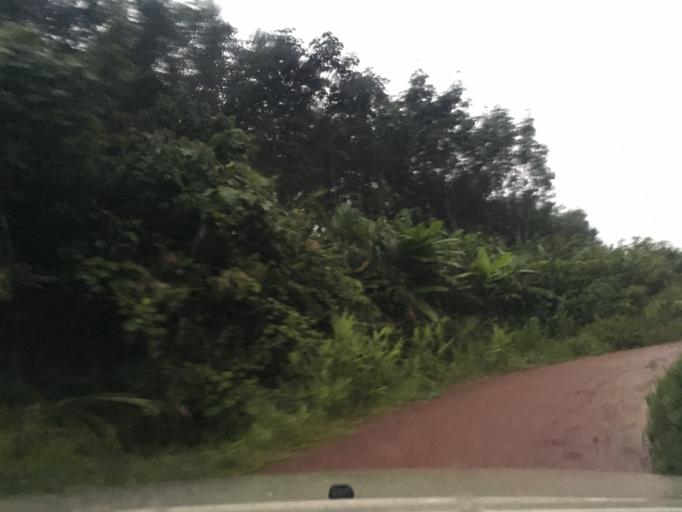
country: LA
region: Oudomxai
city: Muang La
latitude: 21.2490
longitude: 101.9333
